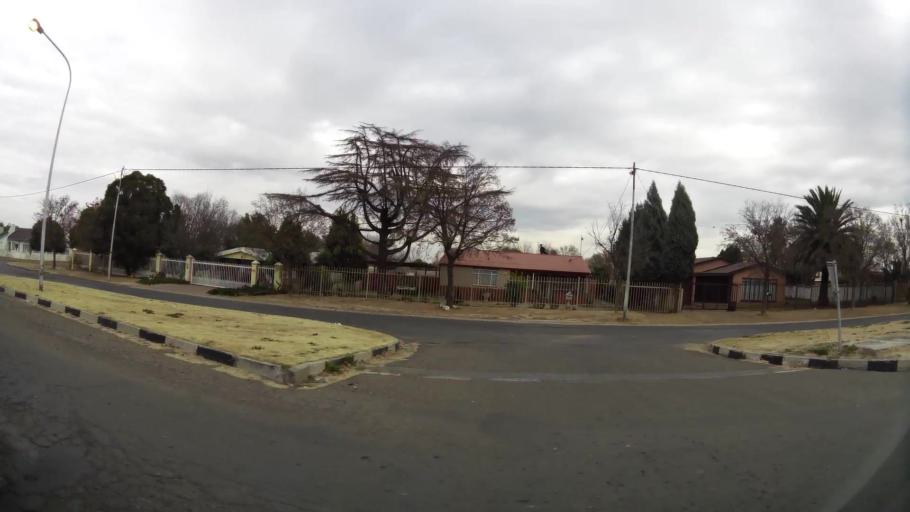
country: ZA
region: Orange Free State
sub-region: Fezile Dabi District Municipality
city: Kroonstad
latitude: -27.6452
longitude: 27.2325
